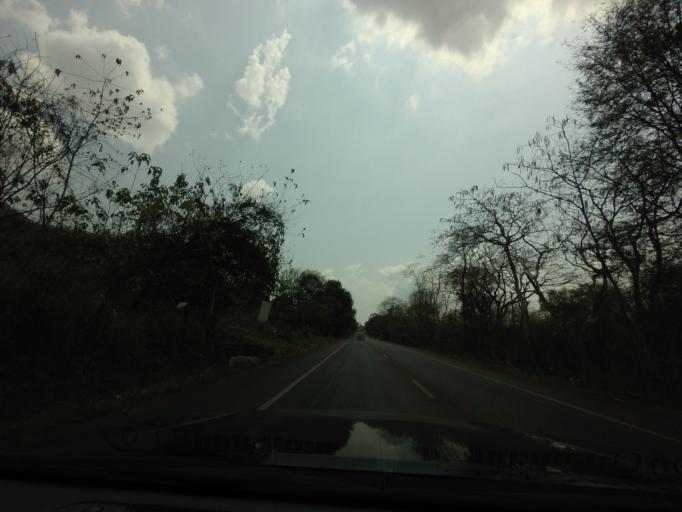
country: TH
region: Kanchanaburi
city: Sai Yok
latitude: 14.1465
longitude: 99.1451
